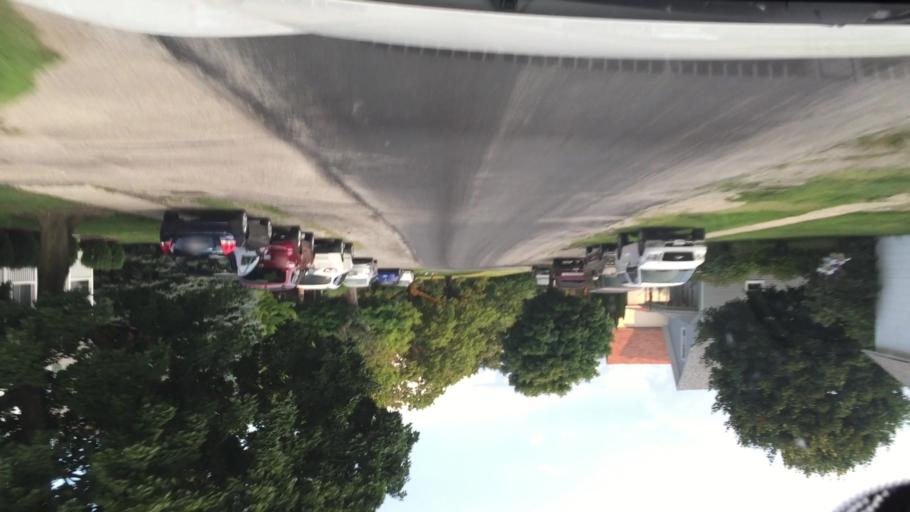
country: US
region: Ohio
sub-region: Champaign County
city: Mechanicsburg
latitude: 40.0009
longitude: -83.6200
